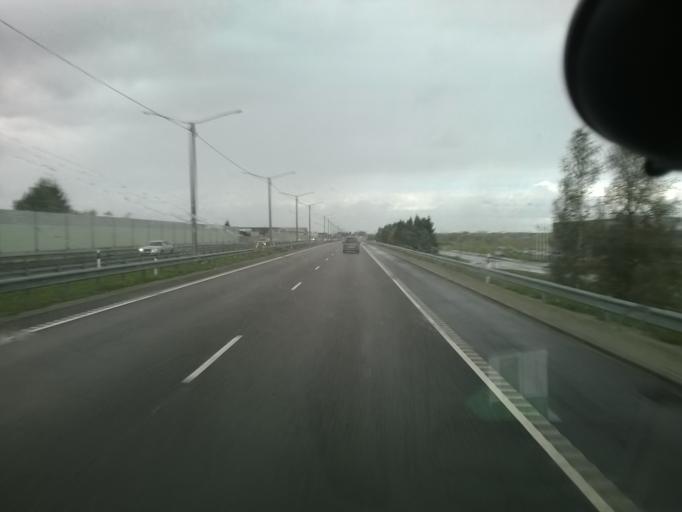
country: EE
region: Harju
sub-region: Rae vald
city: Jueri
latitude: 59.3774
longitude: 24.8454
